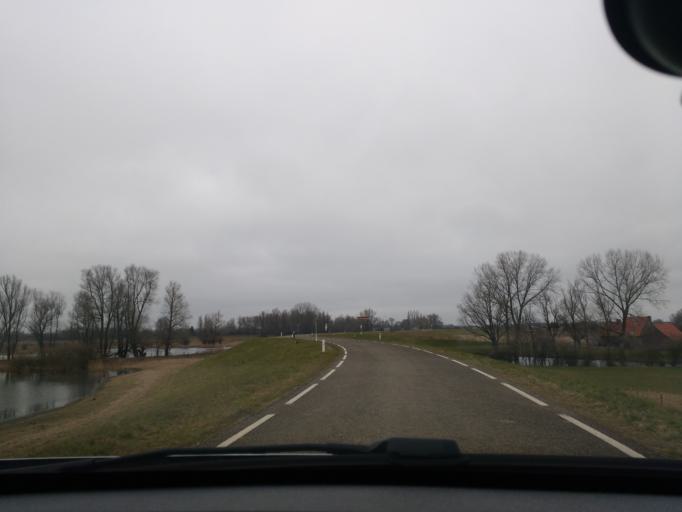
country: NL
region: Gelderland
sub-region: Gemeente Groesbeek
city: Berg en Dal
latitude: 51.8621
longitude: 5.9023
